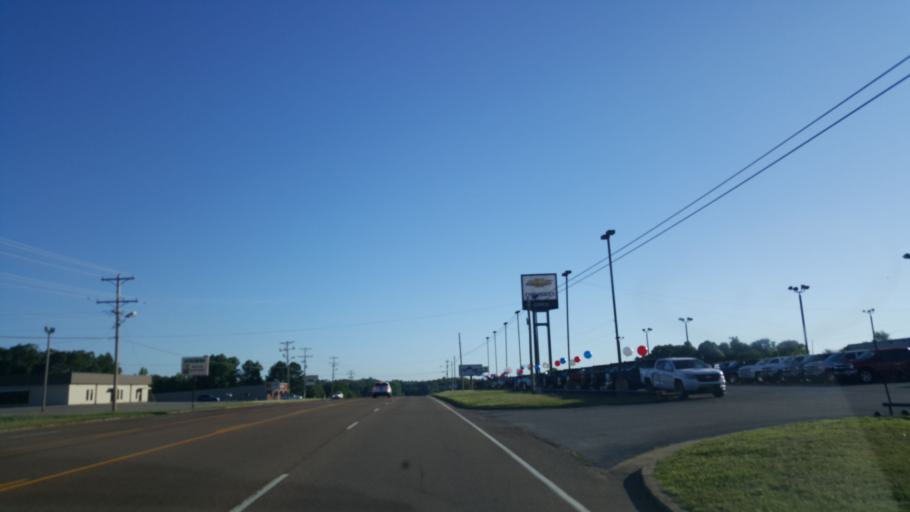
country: US
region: Tennessee
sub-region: Henderson County
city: Lexington
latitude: 35.6383
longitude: -88.4031
